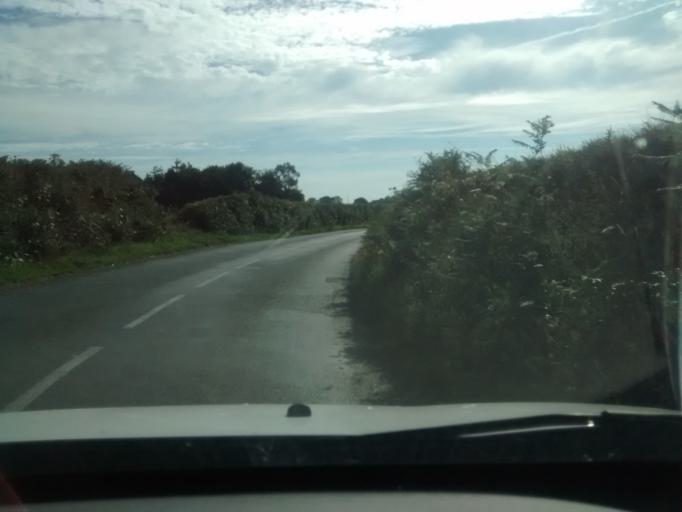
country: FR
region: Brittany
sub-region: Departement des Cotes-d'Armor
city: Plouguiel
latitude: 48.8202
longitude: -3.2607
